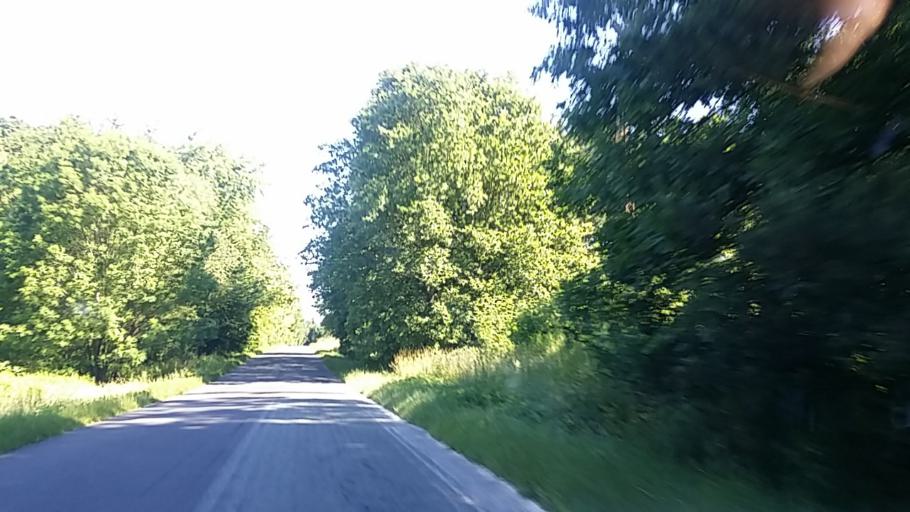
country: HU
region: Zala
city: Zalalovo
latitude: 46.8517
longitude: 16.5026
